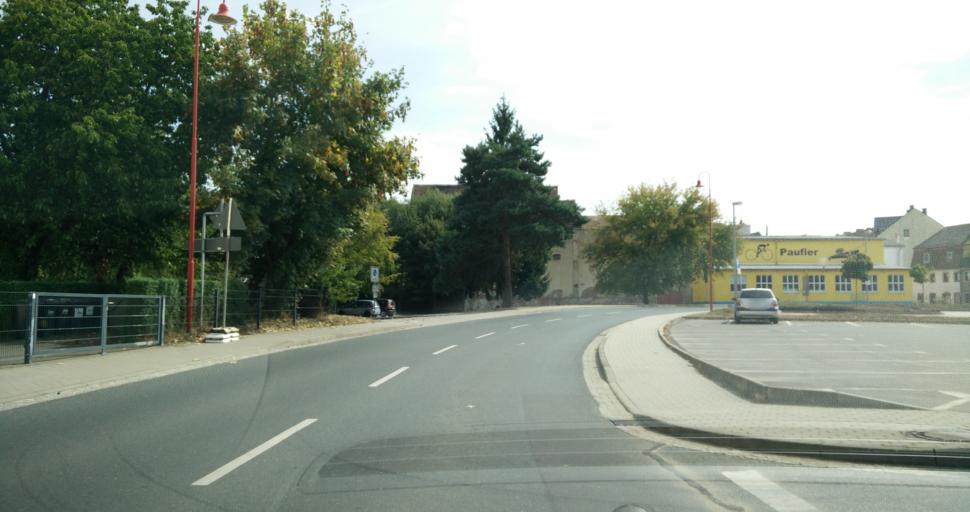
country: DE
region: Saxony
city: Colditz
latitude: 51.1304
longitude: 12.8041
